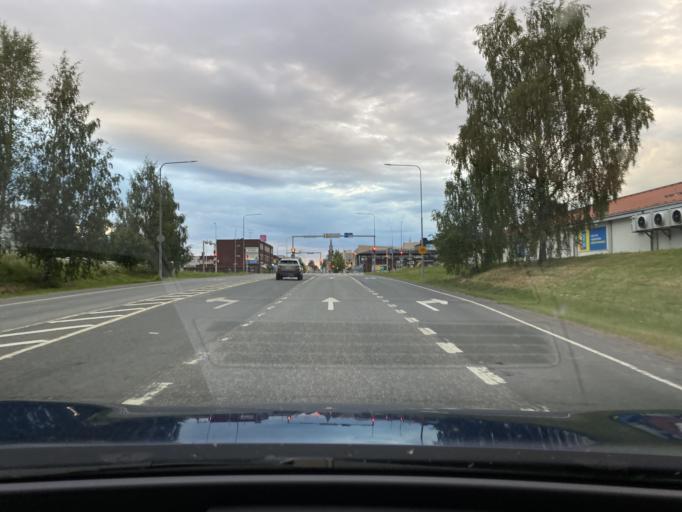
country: FI
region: Northern Ostrobothnia
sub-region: Raahe
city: Raahe
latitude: 64.6822
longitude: 24.4798
